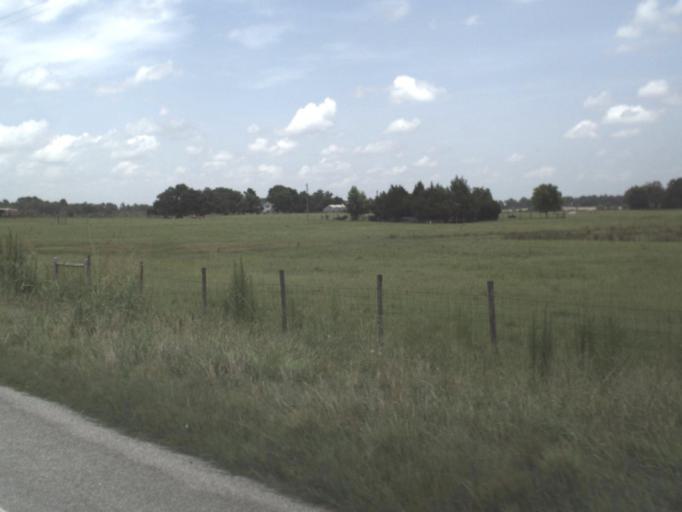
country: US
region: Florida
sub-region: Madison County
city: Madison
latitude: 30.5374
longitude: -83.4247
